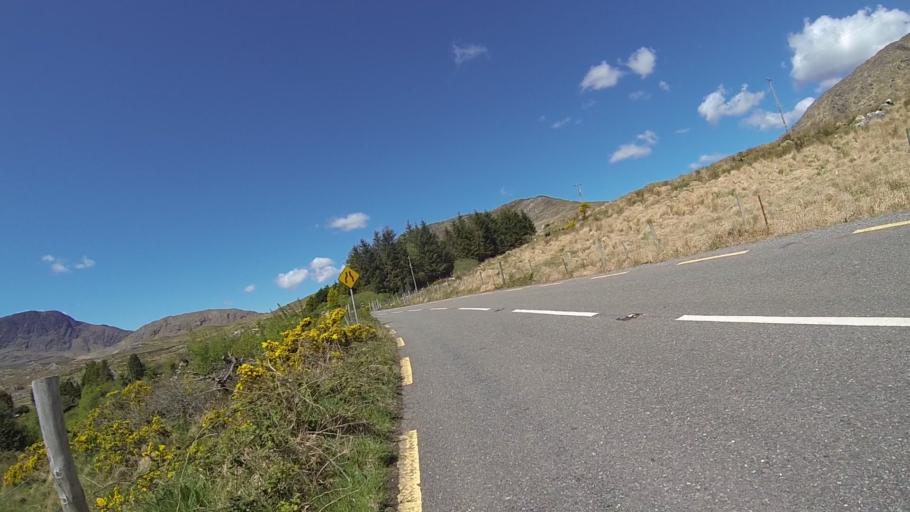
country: IE
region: Munster
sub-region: Ciarrai
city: Kenmare
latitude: 51.9245
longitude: -9.6322
